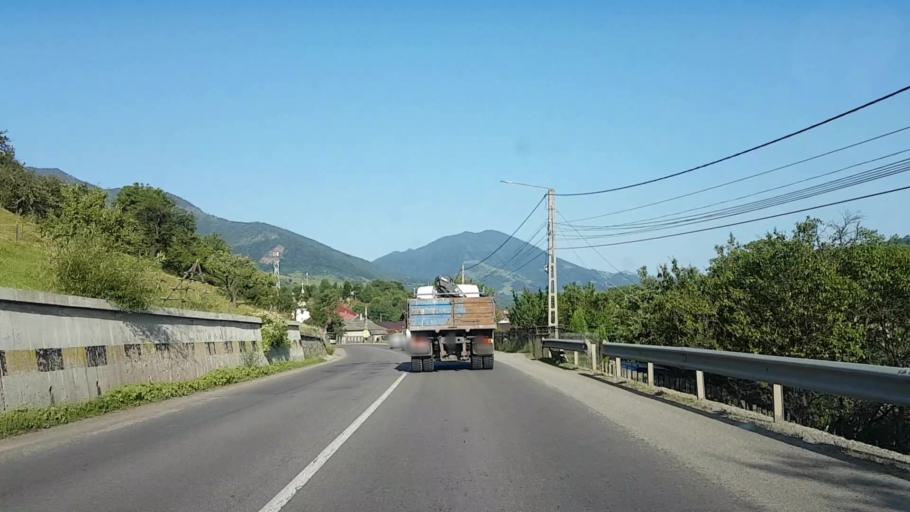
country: RO
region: Bistrita-Nasaud
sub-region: Comuna Tiha Bargaului
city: Tureac
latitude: 47.2296
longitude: 24.8006
